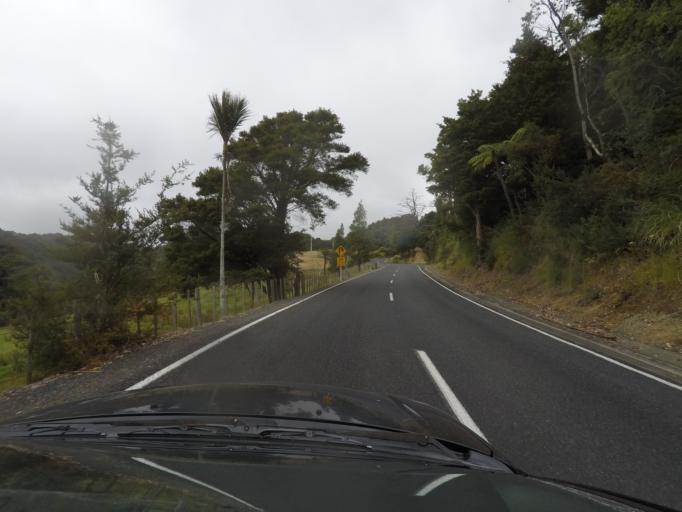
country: NZ
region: Auckland
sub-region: Auckland
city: Warkworth
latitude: -36.2796
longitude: 174.6967
